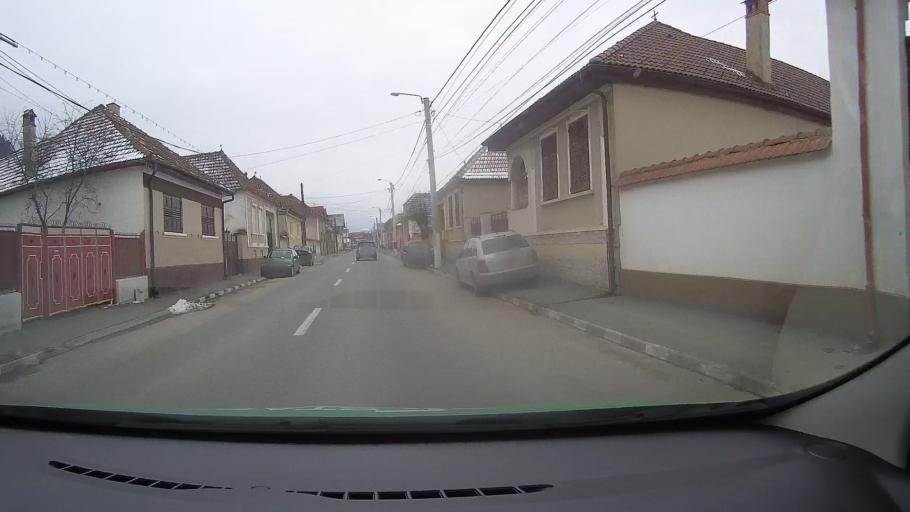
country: RO
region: Brasov
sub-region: Oras Rasnov
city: Rasnov
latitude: 45.5798
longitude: 25.4576
